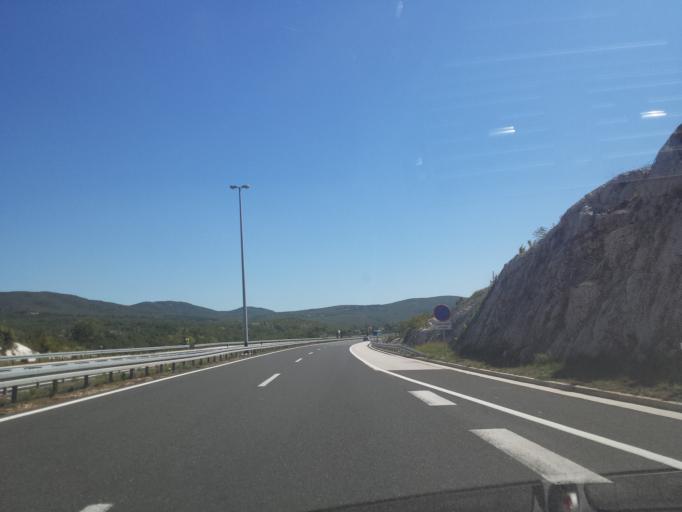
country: HR
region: Splitsko-Dalmatinska
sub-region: Grad Omis
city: Omis
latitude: 43.4926
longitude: 16.7888
